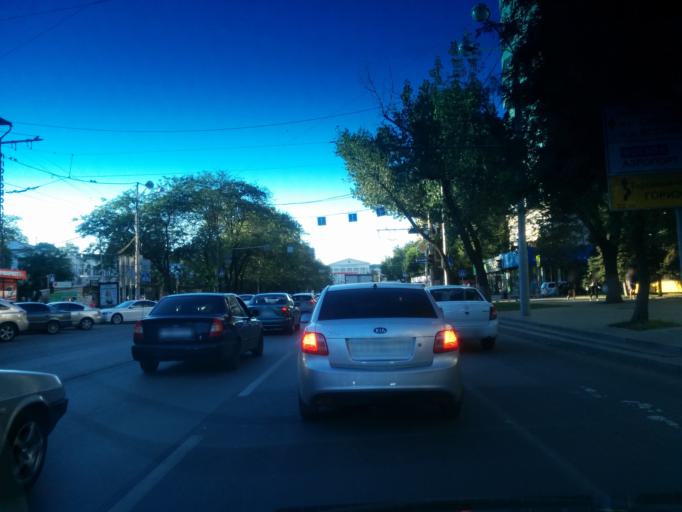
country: RU
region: Rostov
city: Rostov-na-Donu
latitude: 47.2327
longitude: 39.7143
